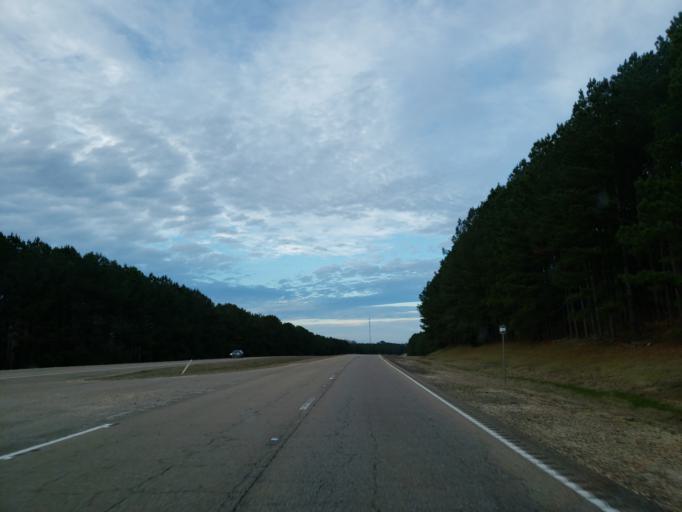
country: US
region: Mississippi
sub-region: Lauderdale County
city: Meridian Station
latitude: 32.6108
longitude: -88.4987
